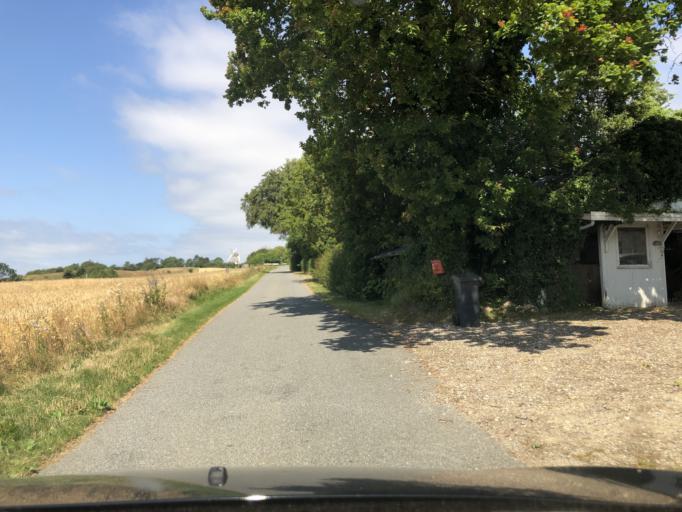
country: DK
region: South Denmark
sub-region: AEro Kommune
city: AEroskobing
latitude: 54.9207
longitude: 10.2882
